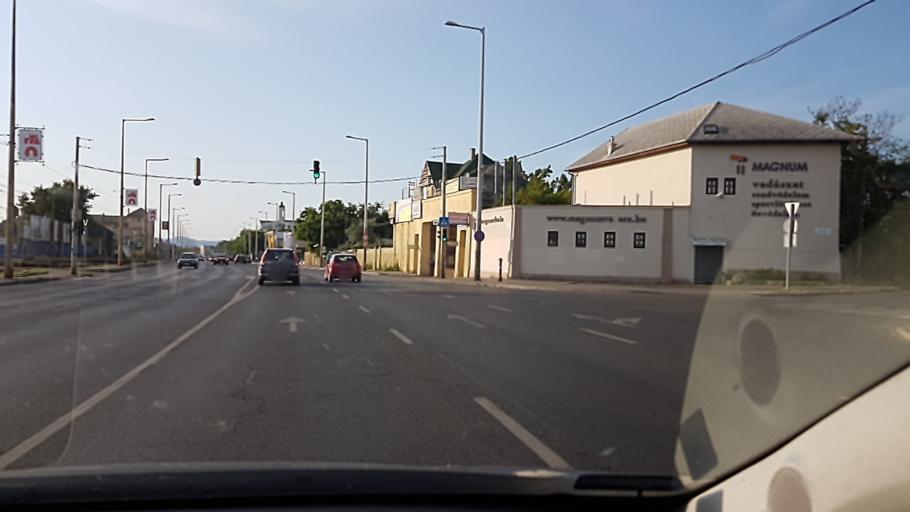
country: HU
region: Budapest
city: Budapest XX. keruelet
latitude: 47.4435
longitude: 19.0931
